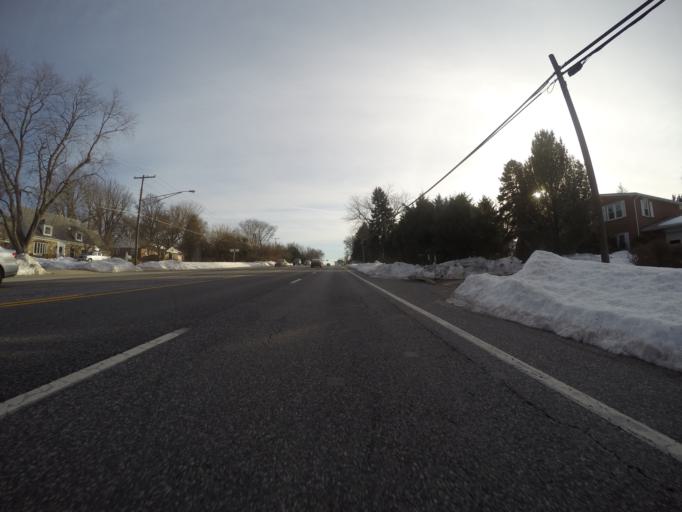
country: US
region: Maryland
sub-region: Baltimore County
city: Hampton
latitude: 39.4180
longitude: -76.5991
